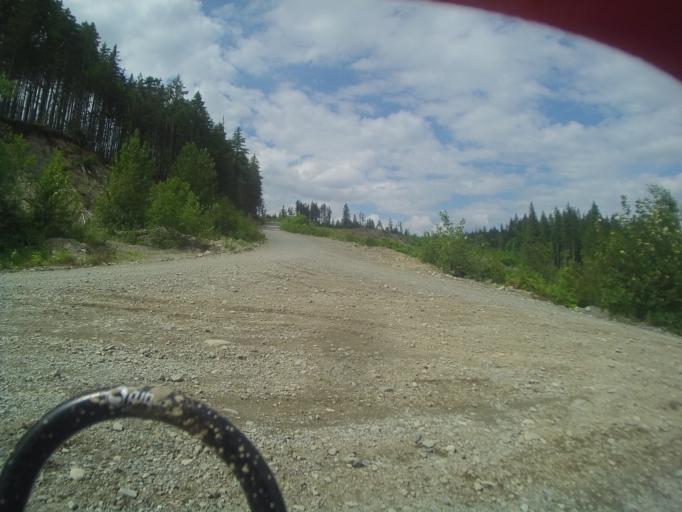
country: CA
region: British Columbia
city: Agassiz
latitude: 49.5398
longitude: -121.8948
